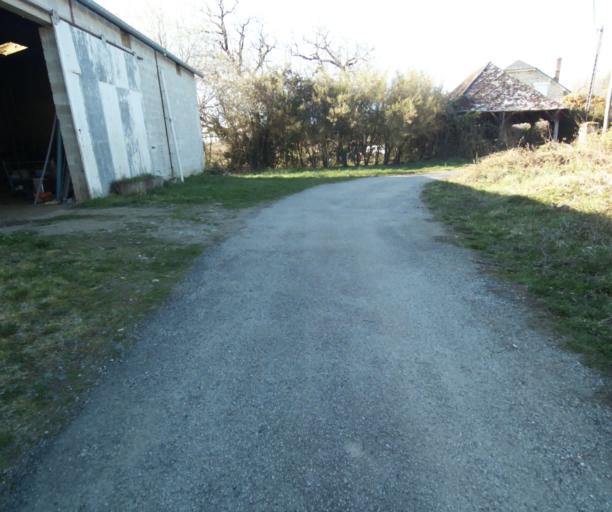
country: FR
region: Limousin
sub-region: Departement de la Correze
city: Seilhac
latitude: 45.3865
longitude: 1.7297
